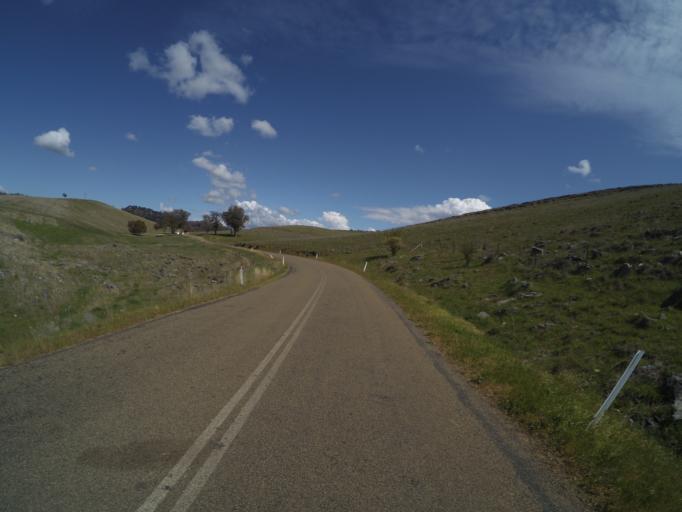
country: AU
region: New South Wales
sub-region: Yass Valley
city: Murrumbateman
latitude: -35.0141
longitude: 148.8533
